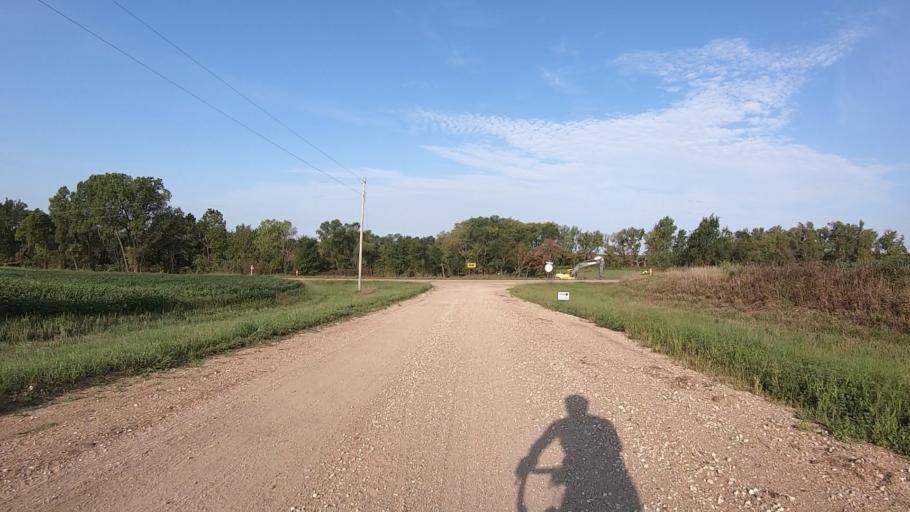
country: US
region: Kansas
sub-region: Marshall County
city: Blue Rapids
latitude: 39.6534
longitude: -96.8619
